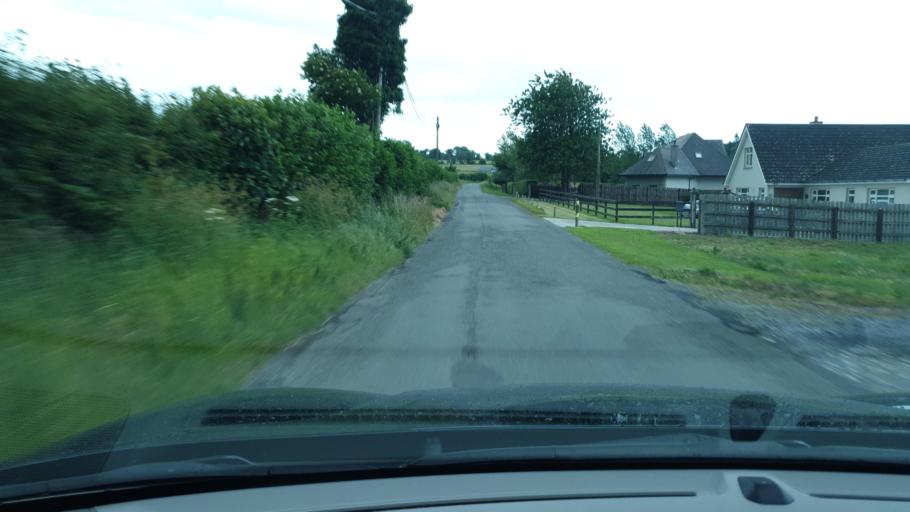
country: IE
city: Kentstown
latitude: 53.5988
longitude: -6.5884
